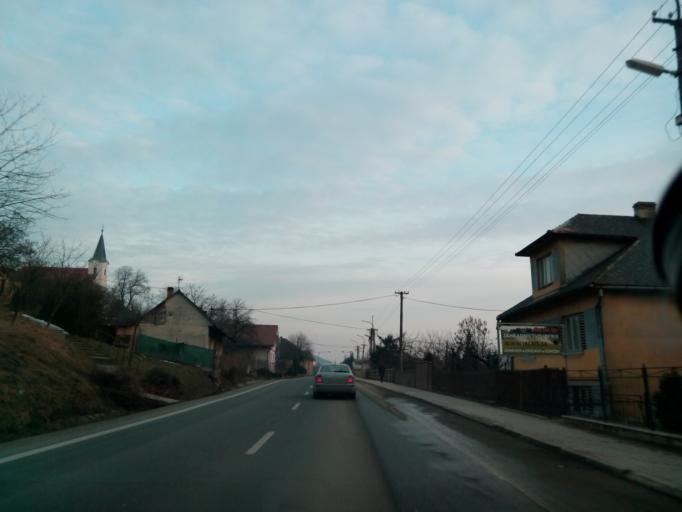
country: SK
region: Presovsky
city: Sabinov
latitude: 49.0710
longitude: 21.1337
